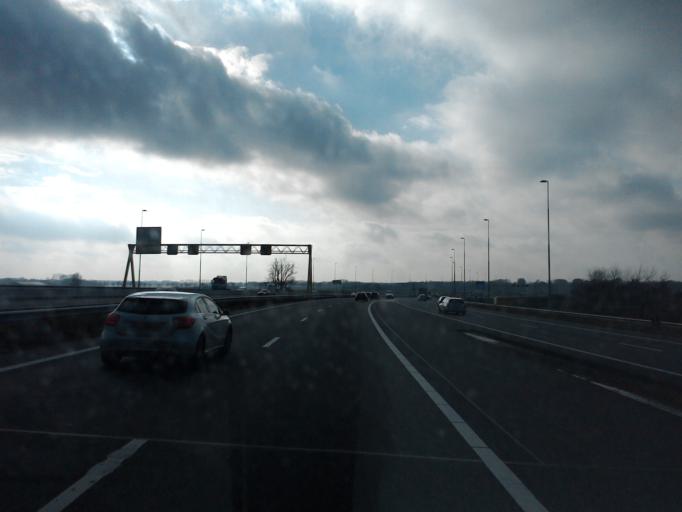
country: NL
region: North Brabant
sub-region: Gemeente Sint-Michielsgestel
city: Sint-Michielsgestel
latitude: 51.6807
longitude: 5.3465
